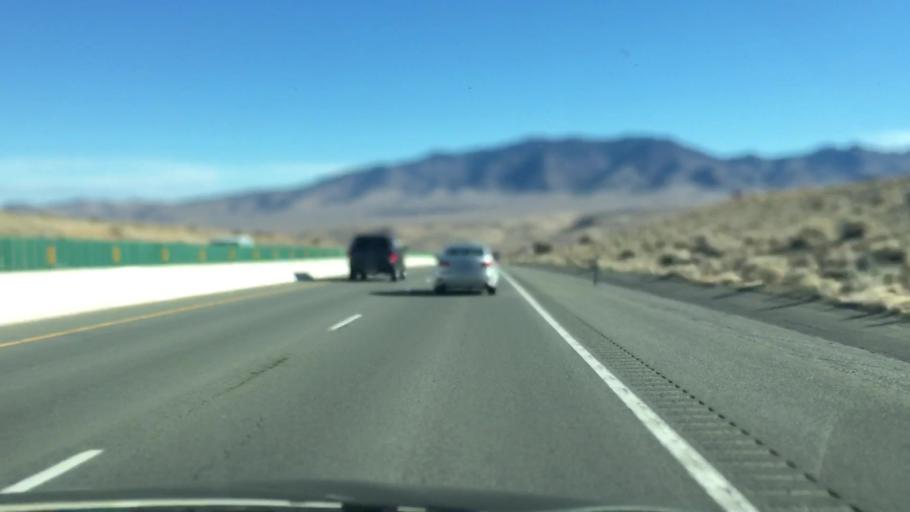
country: US
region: Nevada
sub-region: Lyon County
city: Dayton
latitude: 39.2227
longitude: -119.6230
